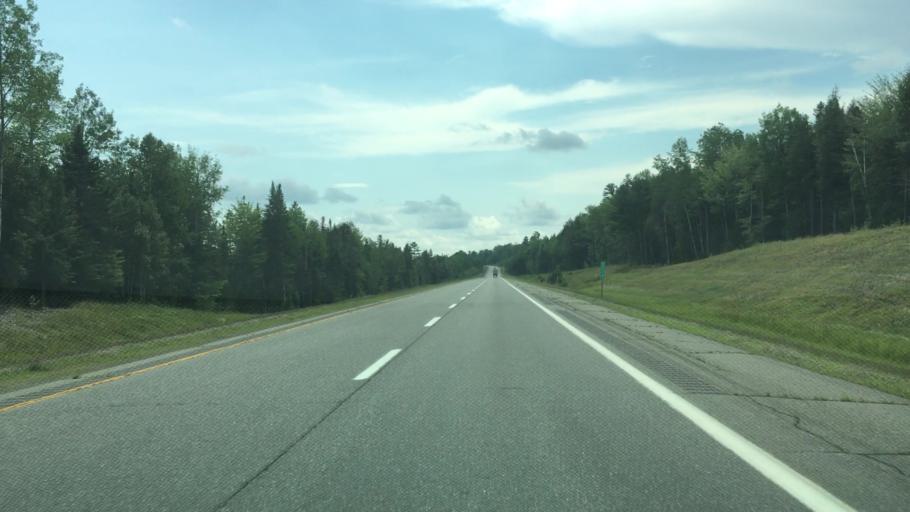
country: US
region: Maine
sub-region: Penobscot County
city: Lincoln
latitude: 45.4688
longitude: -68.5828
